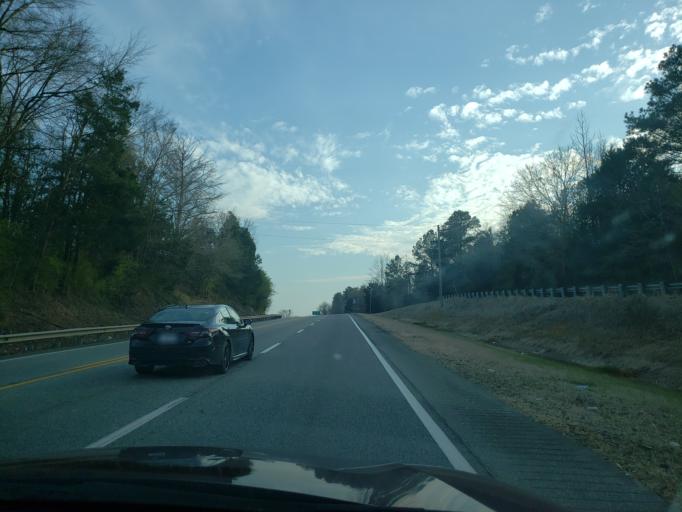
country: US
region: Alabama
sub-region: Hale County
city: Moundville
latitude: 32.9204
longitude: -87.6388
